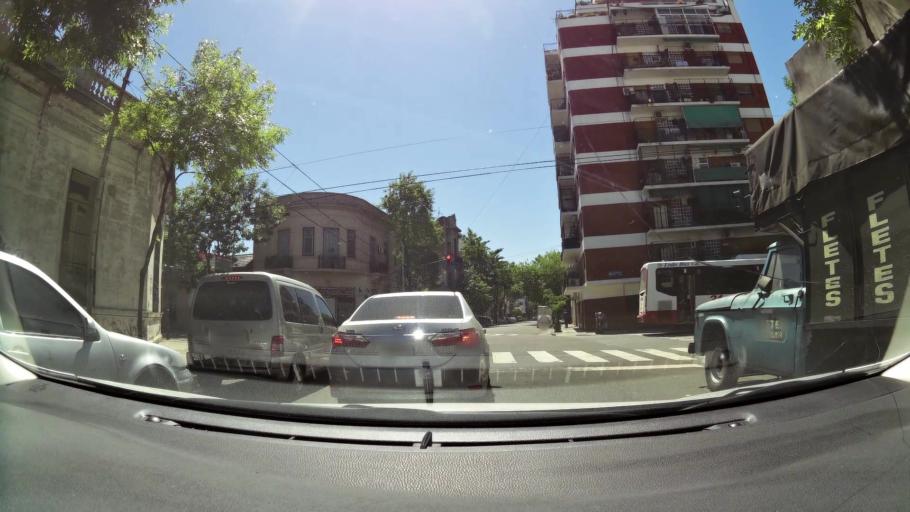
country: AR
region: Buenos Aires F.D.
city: Buenos Aires
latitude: -34.6284
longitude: -58.4087
